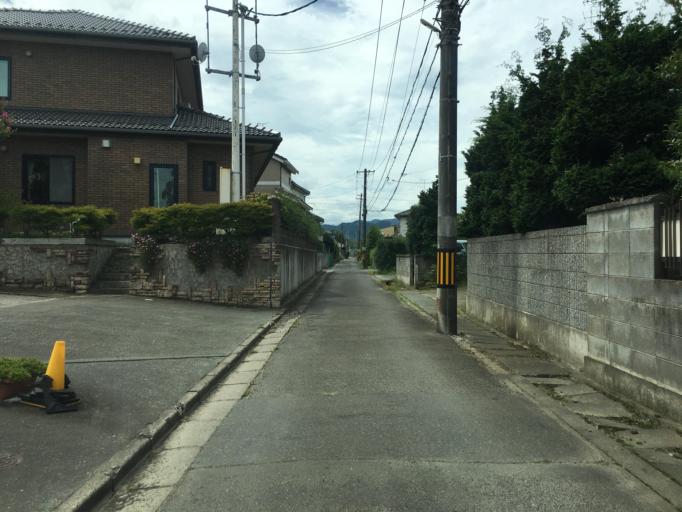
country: JP
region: Miyagi
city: Marumori
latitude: 37.7936
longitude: 140.9168
